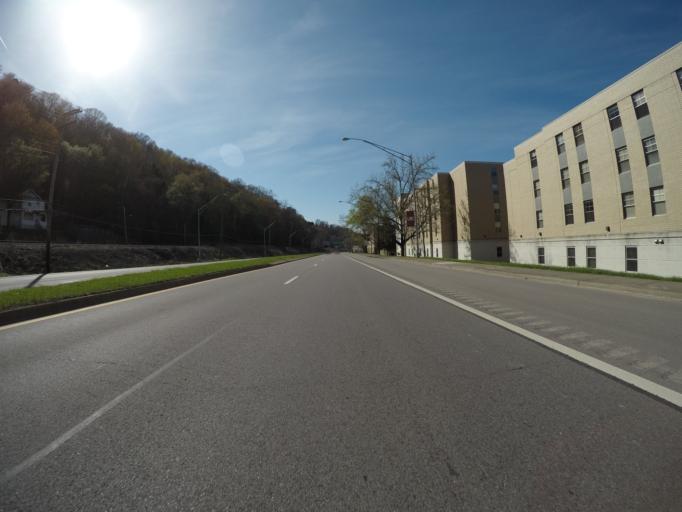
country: US
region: West Virginia
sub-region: Kanawha County
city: Charleston
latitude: 38.3320
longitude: -81.6169
